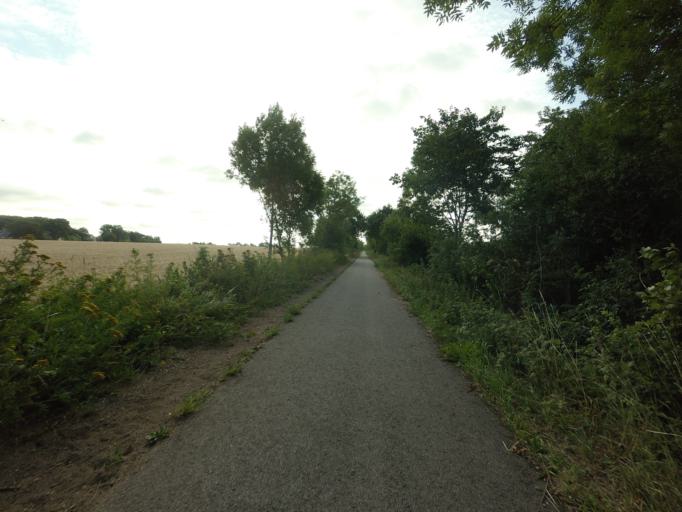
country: SE
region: Skane
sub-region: Hoganas Kommun
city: Hoganas
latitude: 56.1816
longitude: 12.6567
